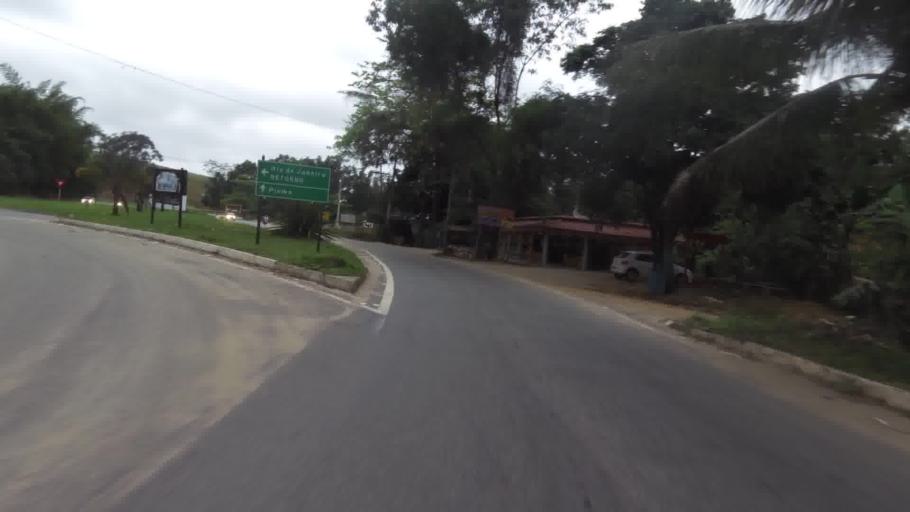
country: BR
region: Espirito Santo
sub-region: Iconha
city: Iconha
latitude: -20.7712
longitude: -40.7636
